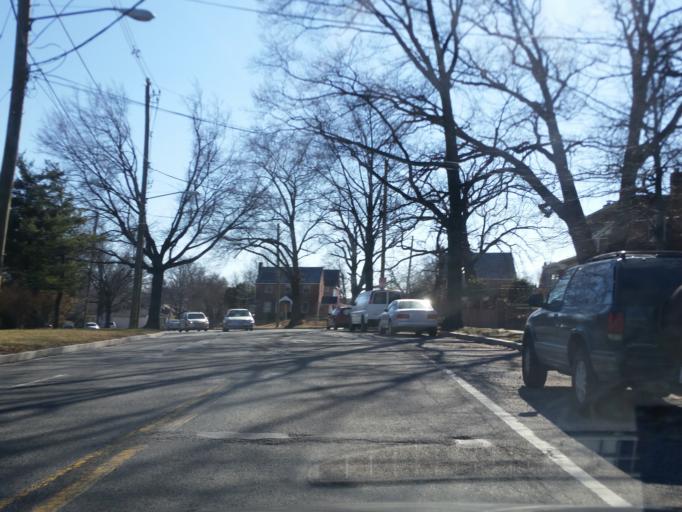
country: US
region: Maryland
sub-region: Montgomery County
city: Takoma Park
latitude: 38.9682
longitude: -77.0141
